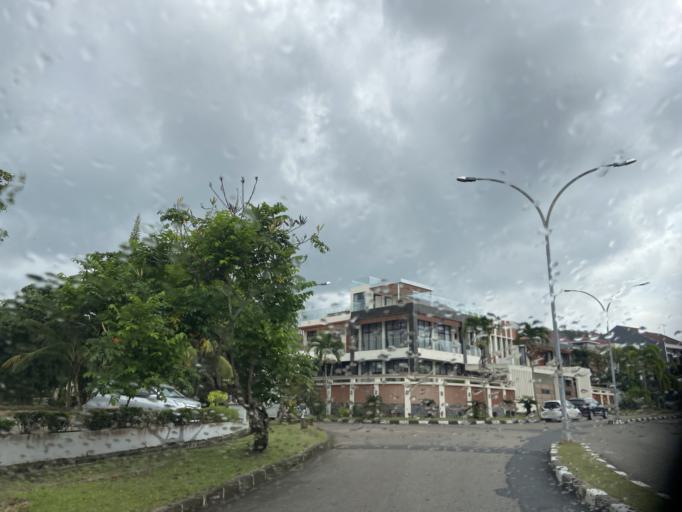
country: SG
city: Singapore
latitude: 1.1043
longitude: 104.0261
